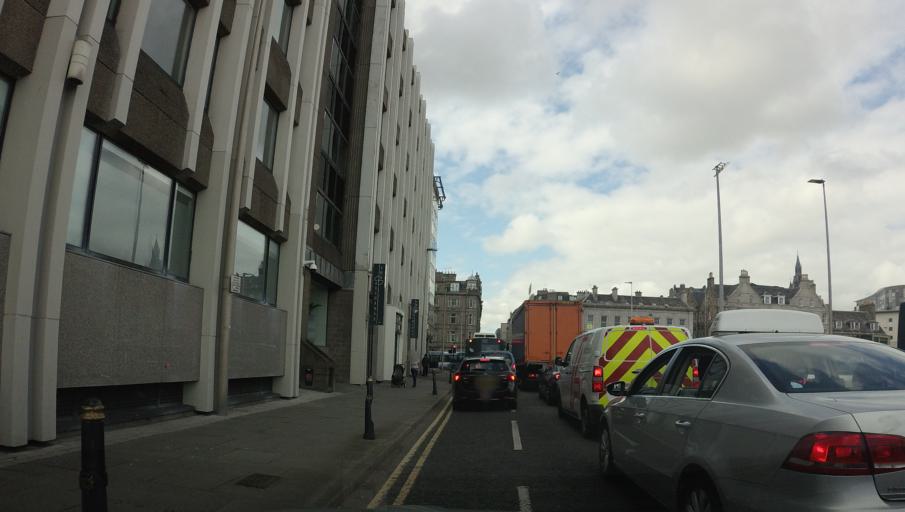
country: GB
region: Scotland
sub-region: Aberdeen City
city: Aberdeen
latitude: 57.1445
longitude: -2.0953
